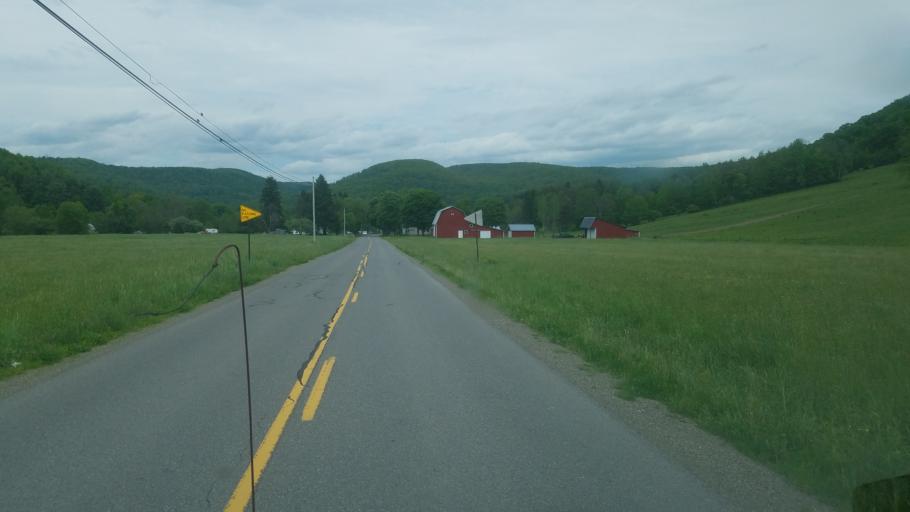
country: US
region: Pennsylvania
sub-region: Tioga County
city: Westfield
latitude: 41.9016
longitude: -77.6051
